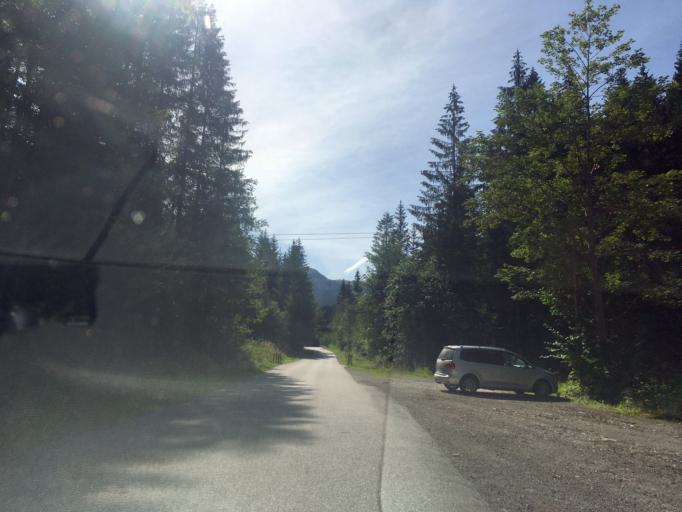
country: AT
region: Salzburg
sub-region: Politischer Bezirk Hallein
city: Abtenau
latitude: 47.5203
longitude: 13.4479
